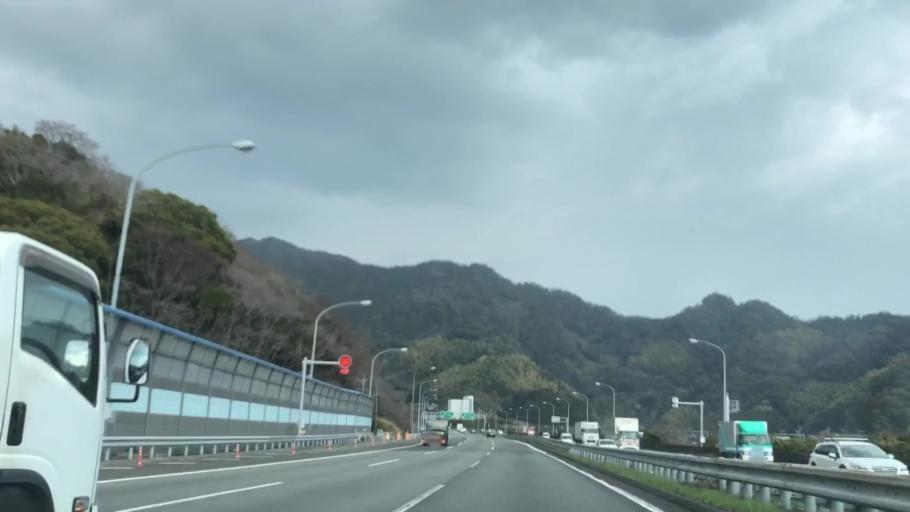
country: JP
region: Shizuoka
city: Yaizu
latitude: 34.8929
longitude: 138.3280
